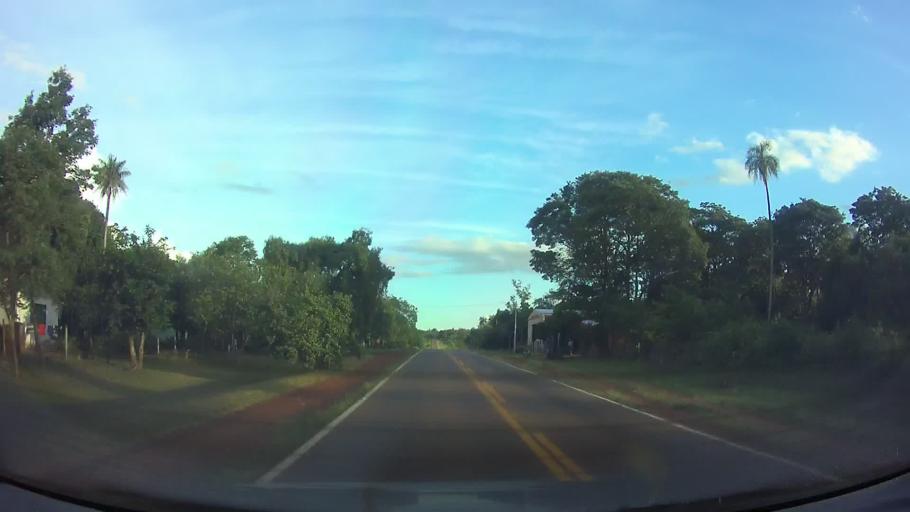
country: PY
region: Paraguari
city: Acahay
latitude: -25.8498
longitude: -57.1425
